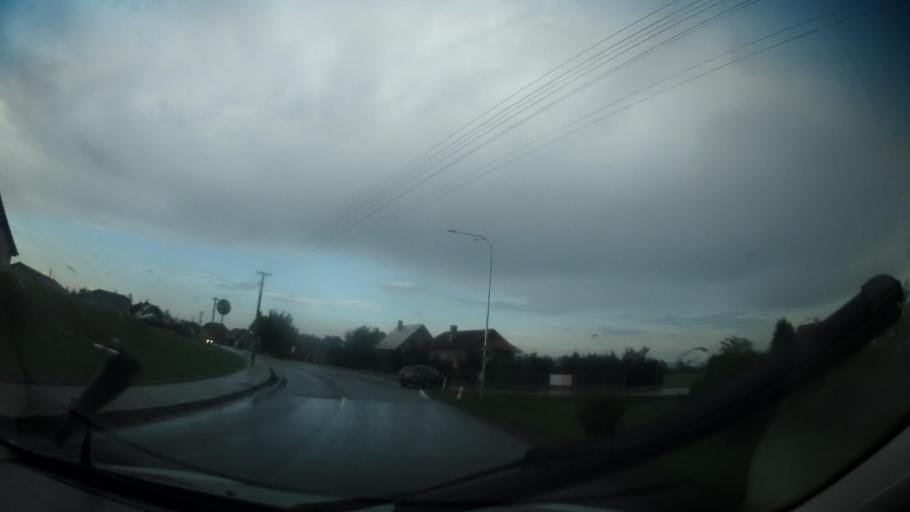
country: CZ
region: Olomoucky
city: Ujezd
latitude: 49.7161
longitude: 17.1587
